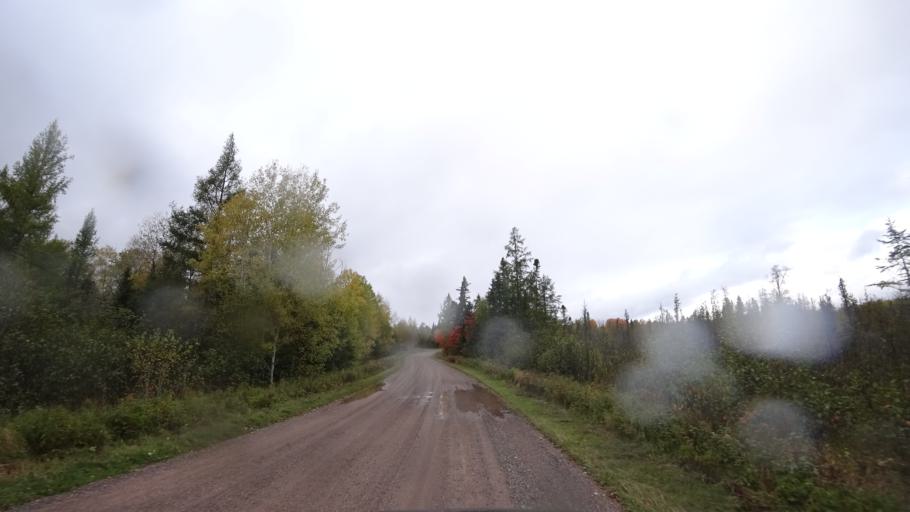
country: US
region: Wisconsin
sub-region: Sawyer County
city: Little Round Lake
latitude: 45.9861
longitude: -90.9992
